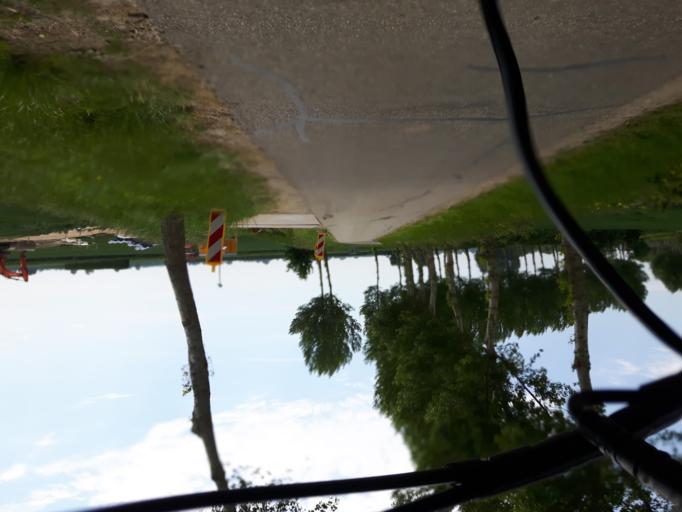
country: NL
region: Zeeland
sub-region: Gemeente Borsele
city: Borssele
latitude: 51.4476
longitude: 3.8099
